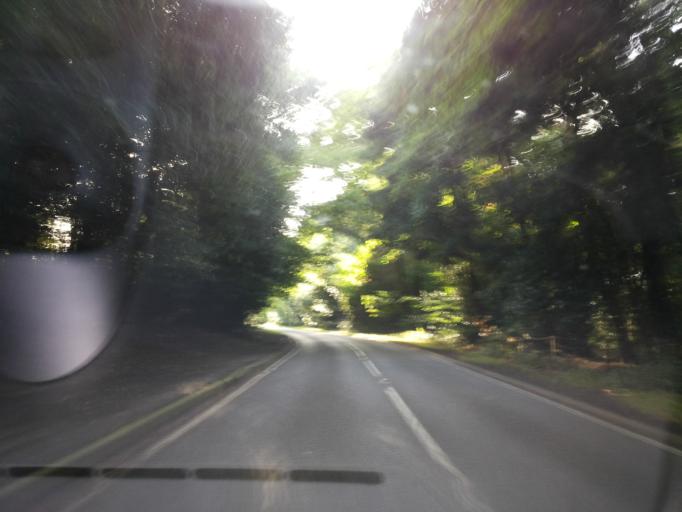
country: GB
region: England
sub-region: Surrey
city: Virginia Water
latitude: 51.3793
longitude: -0.5724
